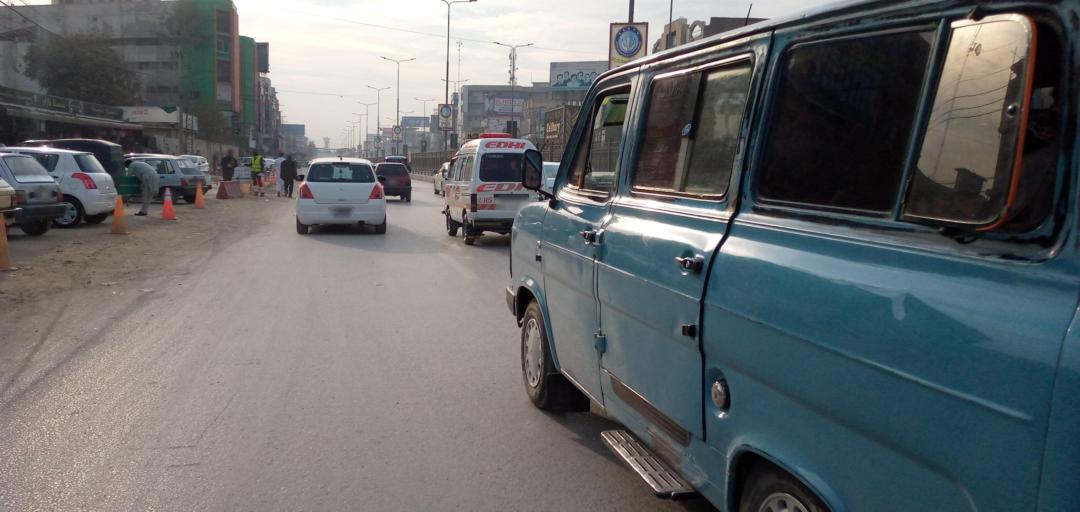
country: PK
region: Khyber Pakhtunkhwa
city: Peshawar
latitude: 34.0021
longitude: 71.5001
